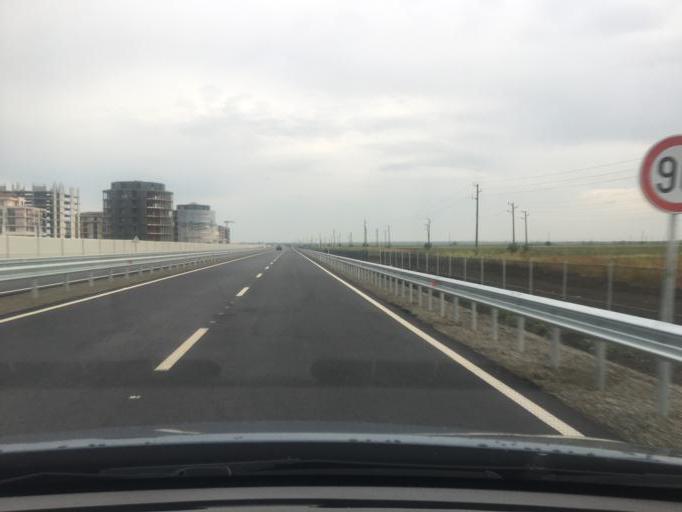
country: BG
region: Burgas
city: Aheloy
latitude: 42.6326
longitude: 27.6351
